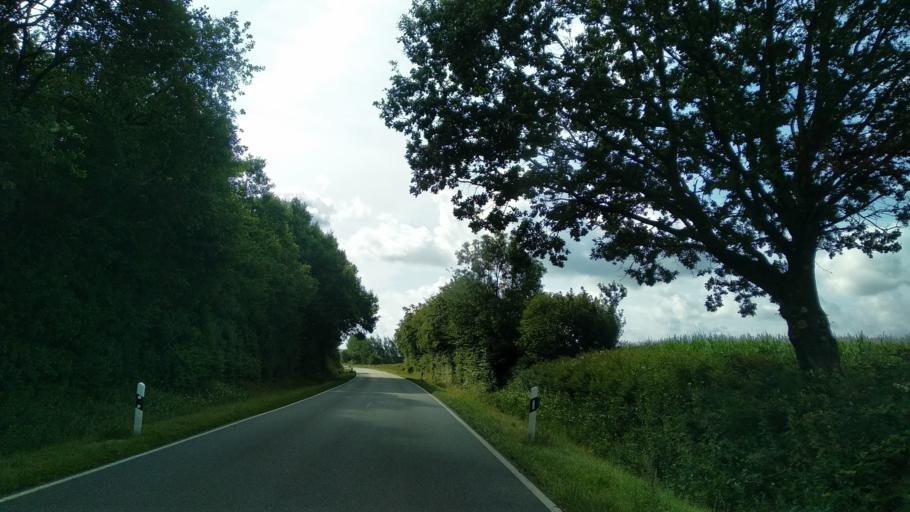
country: DE
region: Schleswig-Holstein
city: Geltorf
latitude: 54.4356
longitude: 9.6053
